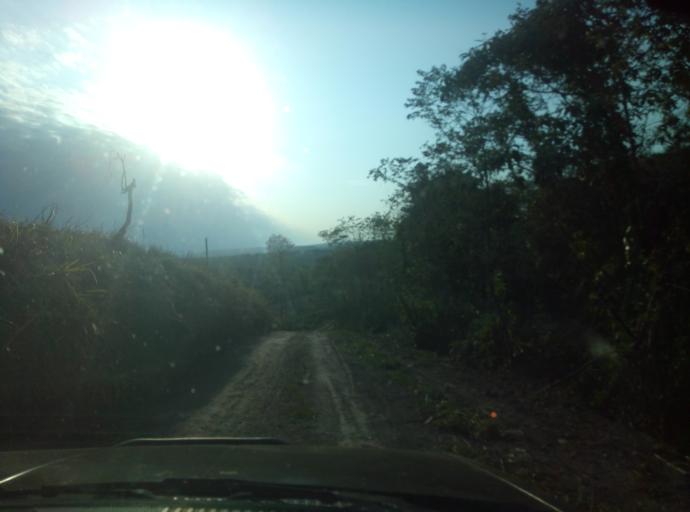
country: PY
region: Caaguazu
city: Doctor Cecilio Baez
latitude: -25.1987
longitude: -56.1324
